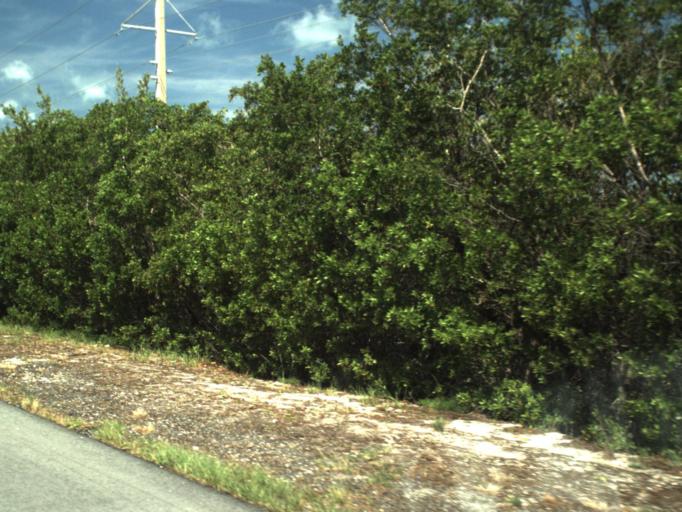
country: US
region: Florida
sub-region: Monroe County
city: Marathon
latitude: 24.7525
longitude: -80.9677
